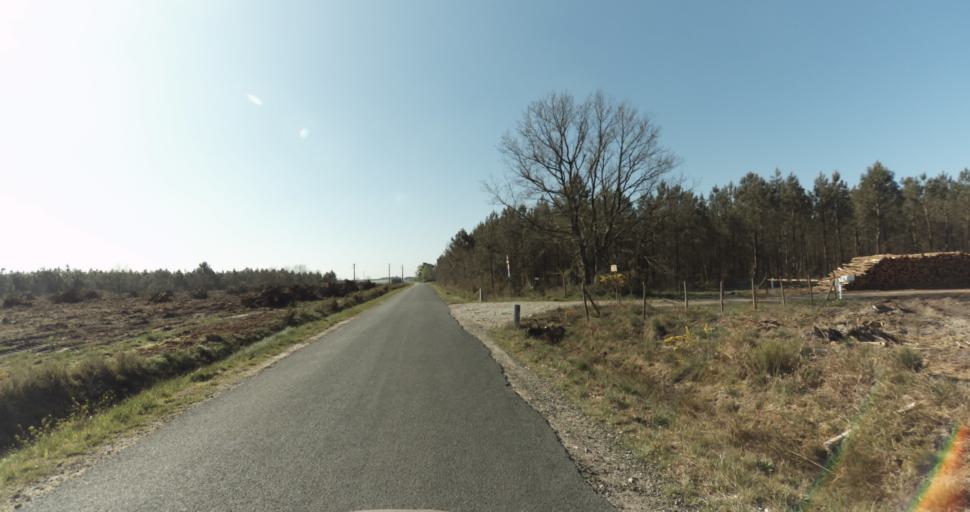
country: FR
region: Aquitaine
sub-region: Departement de la Gironde
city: Marcheprime
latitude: 44.7773
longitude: -0.8594
